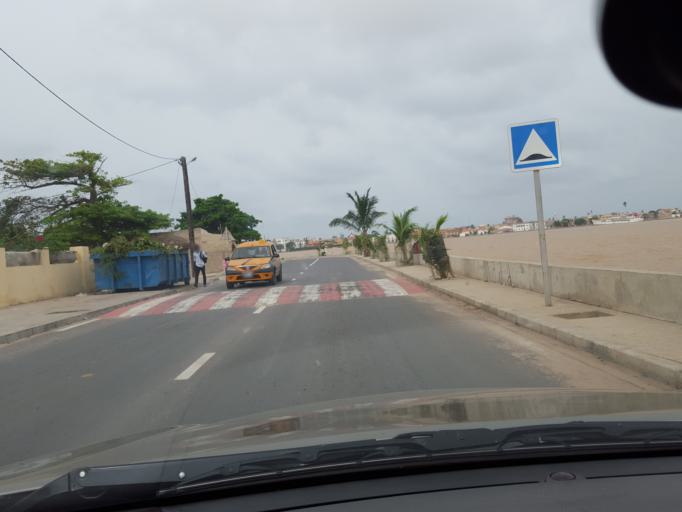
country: SN
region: Saint-Louis
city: Saint-Louis
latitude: 16.0300
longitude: -16.4956
